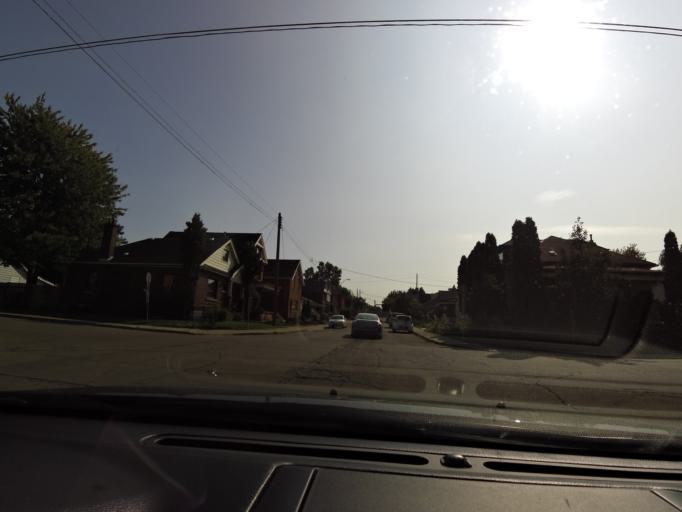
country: CA
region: Ontario
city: Hamilton
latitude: 43.2668
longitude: -79.8590
